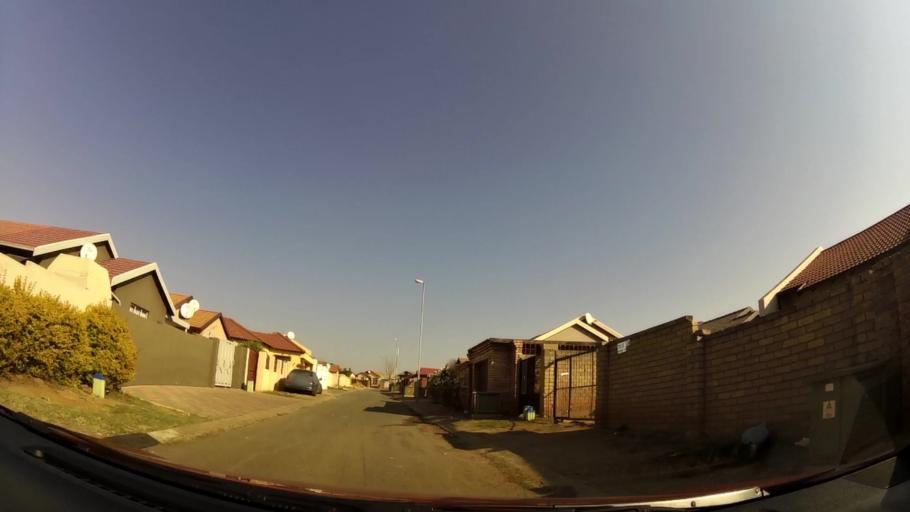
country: ZA
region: Gauteng
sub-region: City of Johannesburg Metropolitan Municipality
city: Soweto
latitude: -26.2960
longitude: 27.9513
